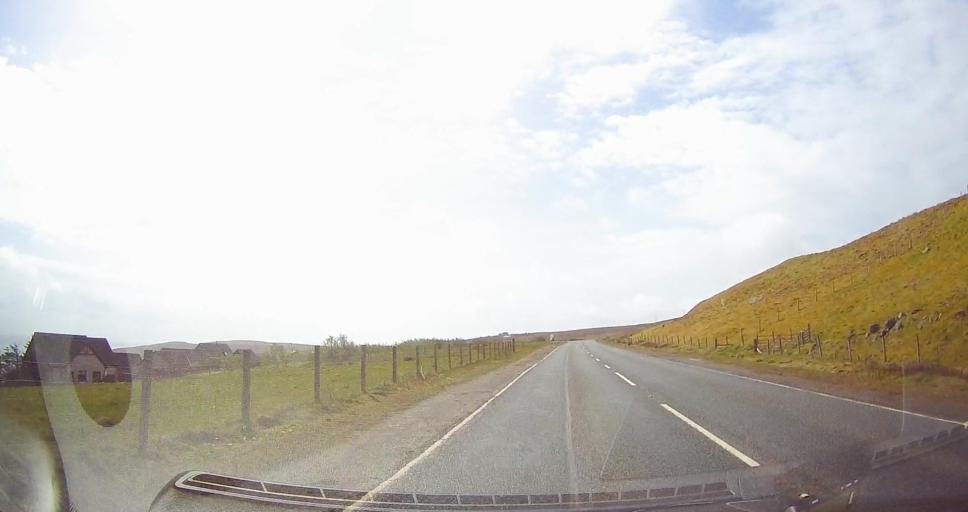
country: GB
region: Scotland
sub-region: Shetland Islands
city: Lerwick
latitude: 60.1301
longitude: -1.2151
